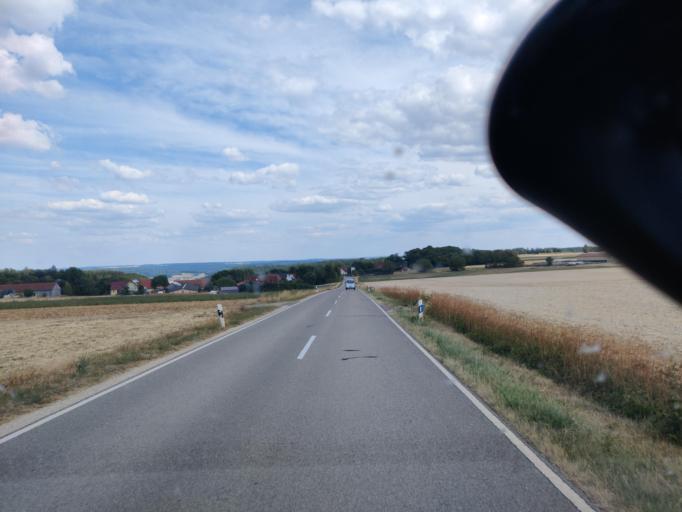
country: DE
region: Bavaria
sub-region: Regierungsbezirk Mittelfranken
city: Thalmassing
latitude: 49.0775
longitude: 11.1802
